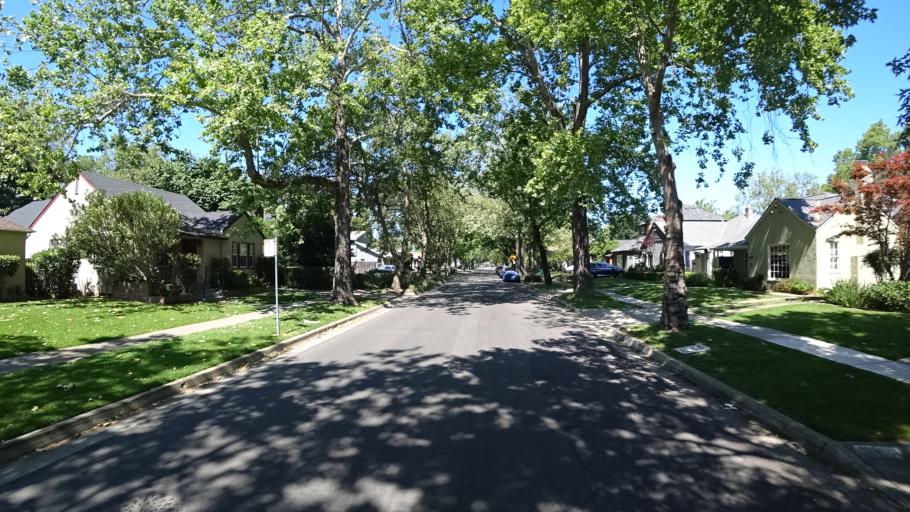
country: US
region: California
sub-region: Sacramento County
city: Sacramento
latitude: 38.5520
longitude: -121.4923
